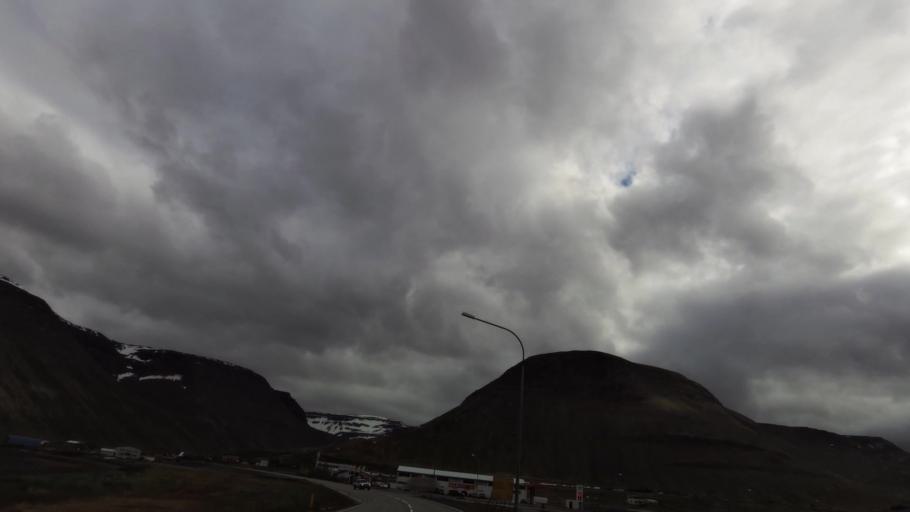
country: IS
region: Westfjords
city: Isafjoerdur
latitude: 66.0619
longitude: -23.1743
